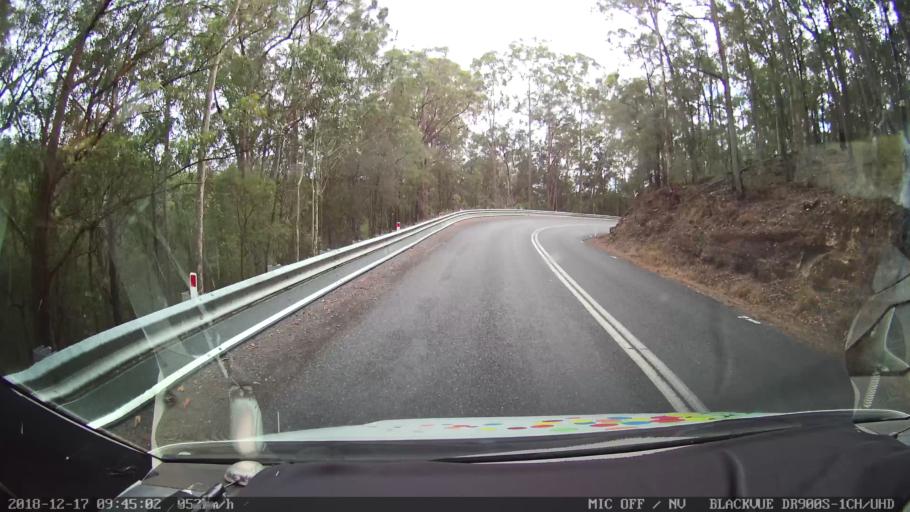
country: AU
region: New South Wales
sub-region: Tenterfield Municipality
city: Carrolls Creek
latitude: -28.9263
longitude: 152.3264
